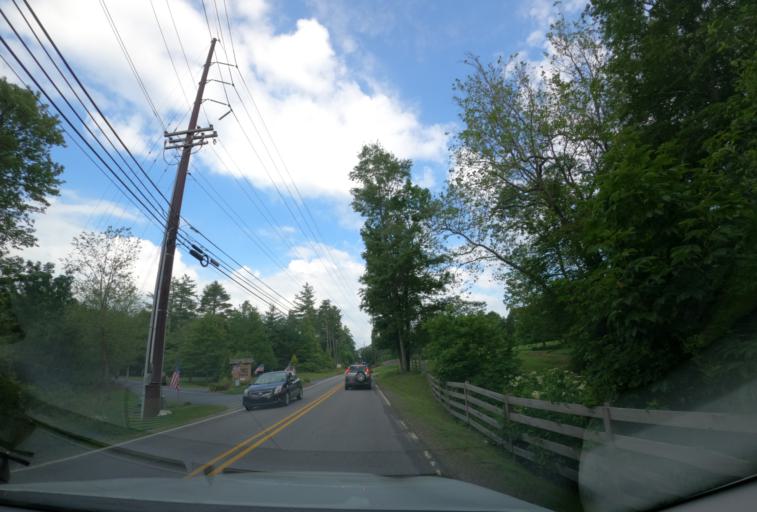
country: US
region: North Carolina
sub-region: Macon County
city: Franklin
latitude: 35.0859
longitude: -83.1786
